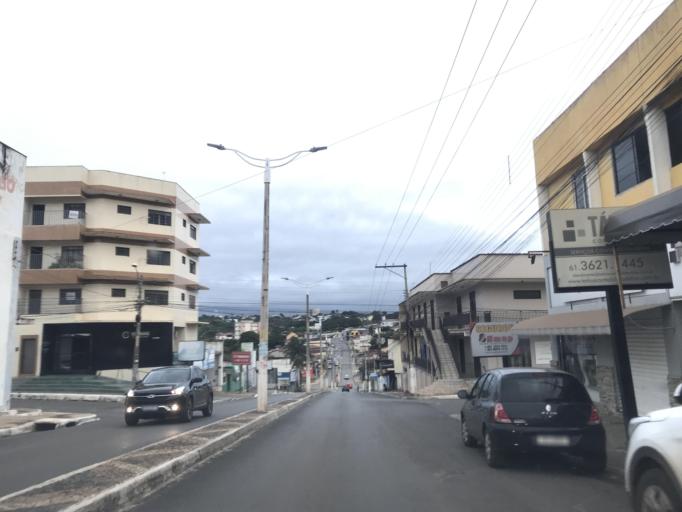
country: BR
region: Goias
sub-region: Luziania
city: Luziania
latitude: -16.2500
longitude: -47.9535
